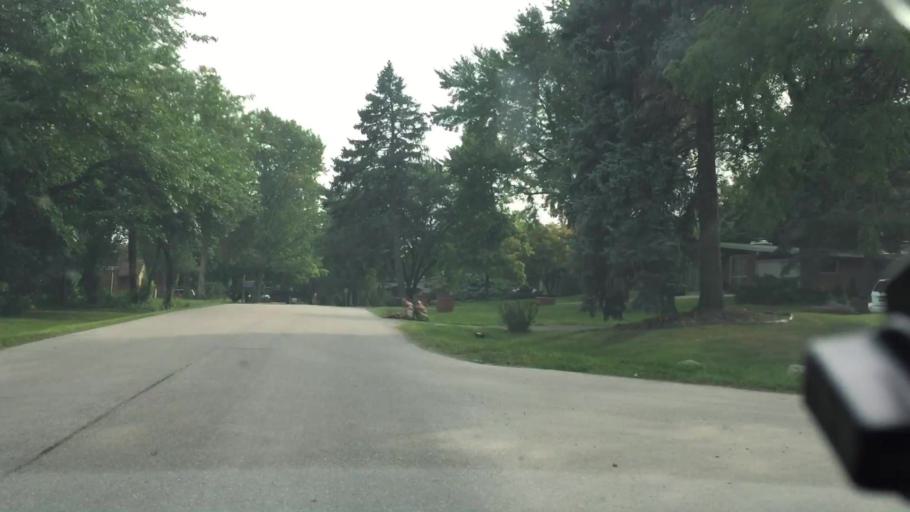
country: US
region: Michigan
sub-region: Oakland County
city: Sylvan Lake
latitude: 42.6016
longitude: -83.2929
